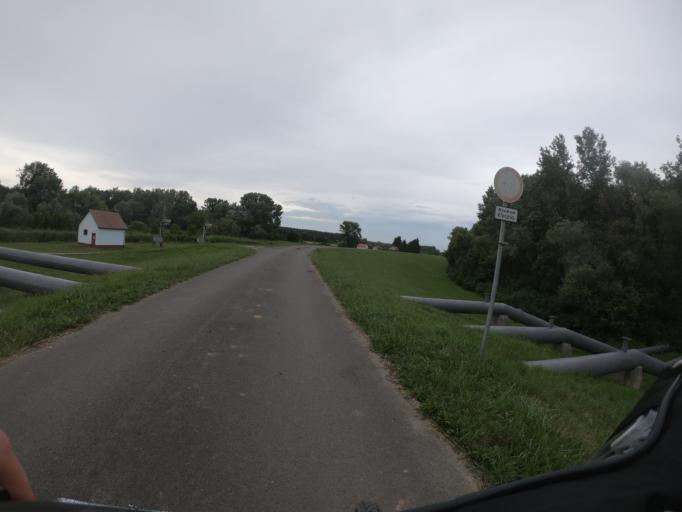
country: HU
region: Hajdu-Bihar
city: Tiszacsege
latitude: 47.7295
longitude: 20.9557
